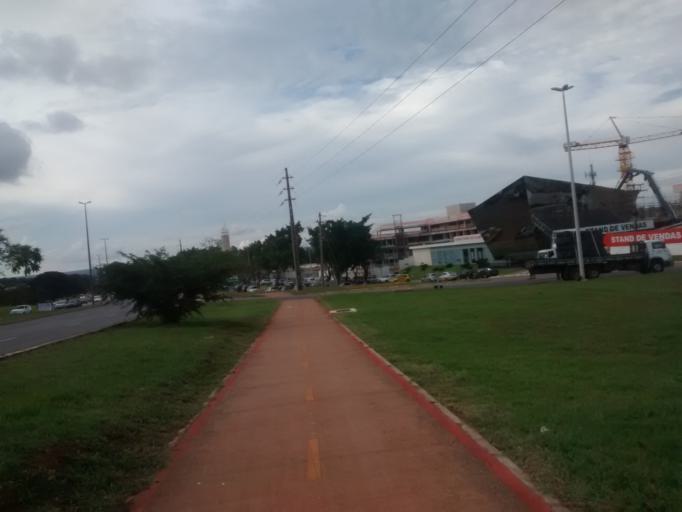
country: BR
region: Federal District
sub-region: Brasilia
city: Brasilia
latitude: -15.7901
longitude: -47.8733
